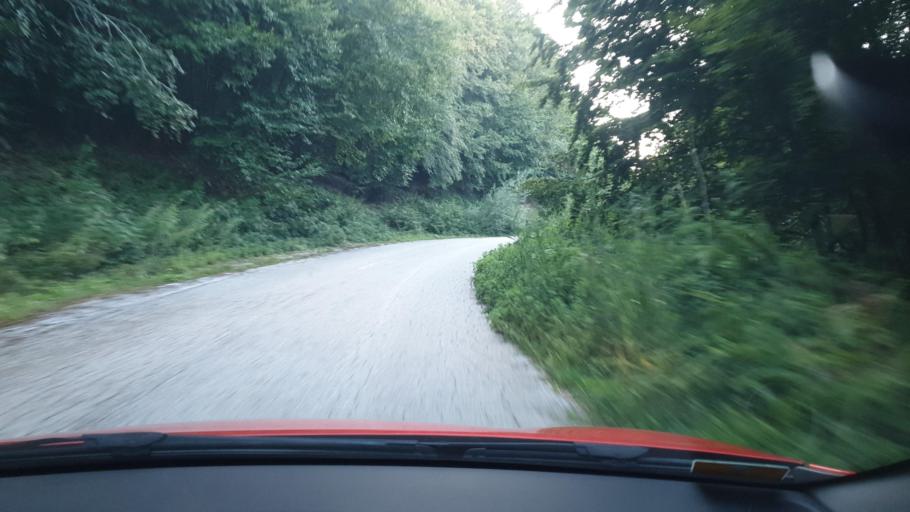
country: GR
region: Central Macedonia
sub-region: Nomos Chalkidikis
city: Galatista
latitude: 40.5097
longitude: 23.2542
